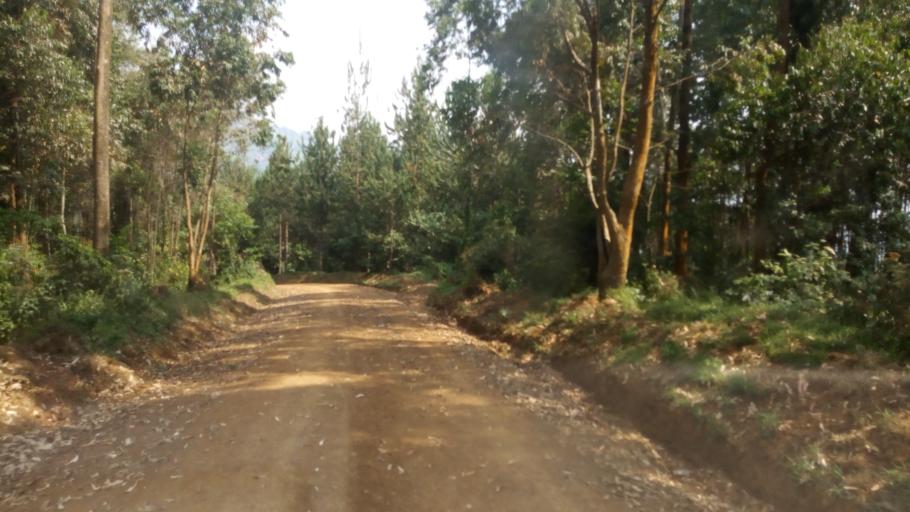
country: UG
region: Western Region
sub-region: Kanungu District
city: Ntungamo
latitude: -1.0229
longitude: 29.5867
